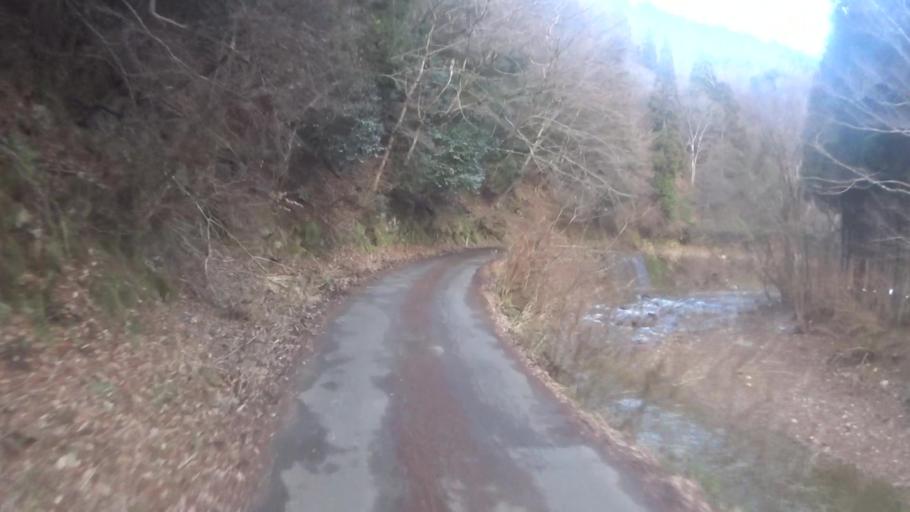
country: JP
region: Kyoto
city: Maizuru
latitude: 35.3983
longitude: 135.4877
